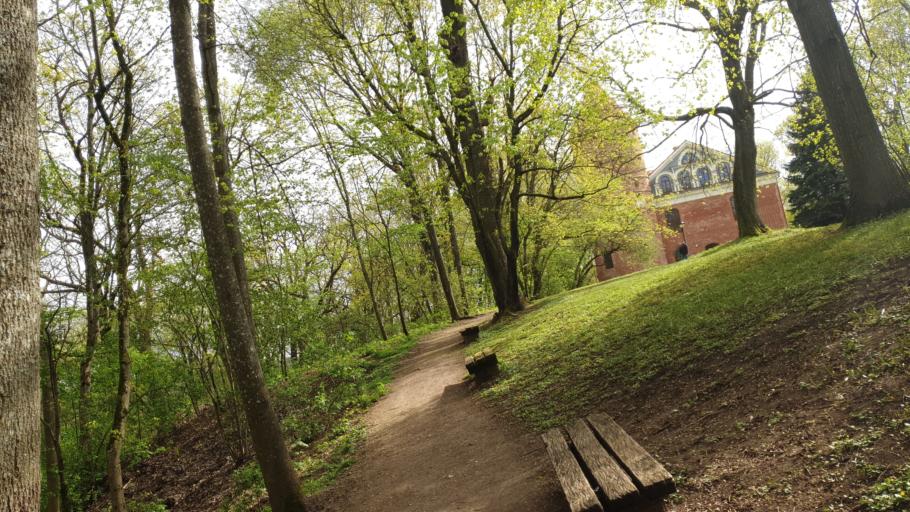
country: LT
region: Kauno apskritis
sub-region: Kauno rajonas
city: Akademija (Kaunas)
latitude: 54.9441
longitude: 23.7846
